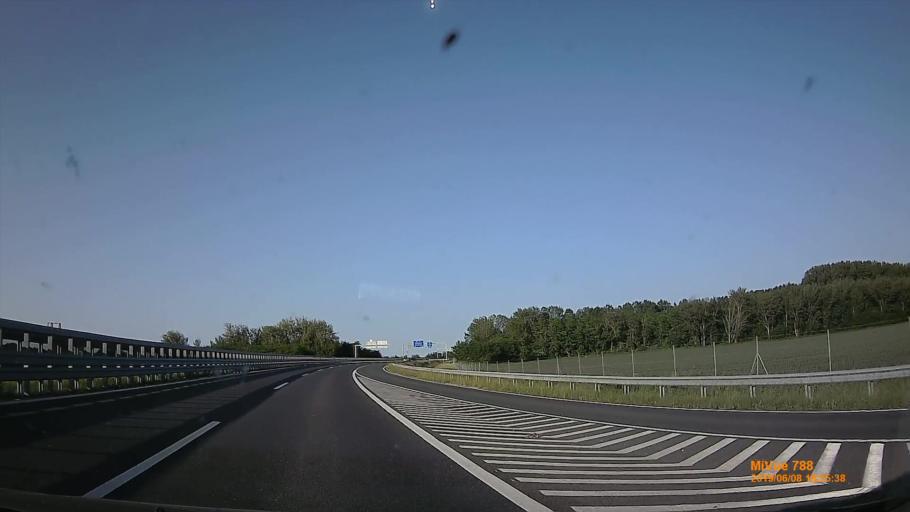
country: HU
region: Gyor-Moson-Sopron
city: Csorna
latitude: 47.6201
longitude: 17.2827
